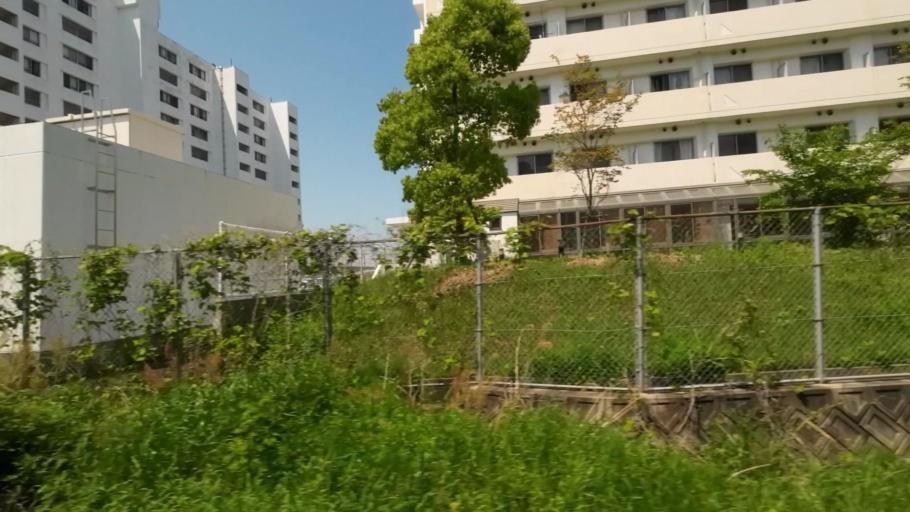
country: JP
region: Ehime
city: Hojo
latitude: 34.0726
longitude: 132.9321
